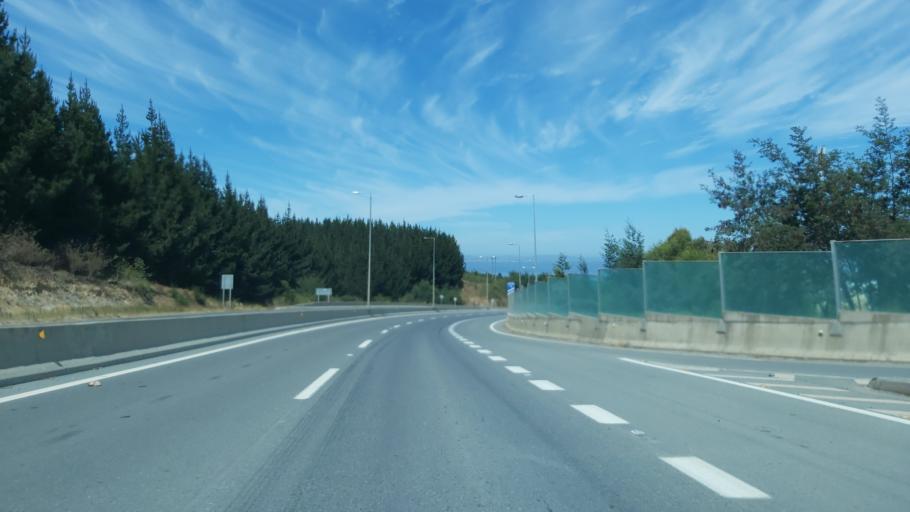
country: CL
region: Biobio
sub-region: Provincia de Concepcion
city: Lota
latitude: -37.0984
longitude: -73.1436
